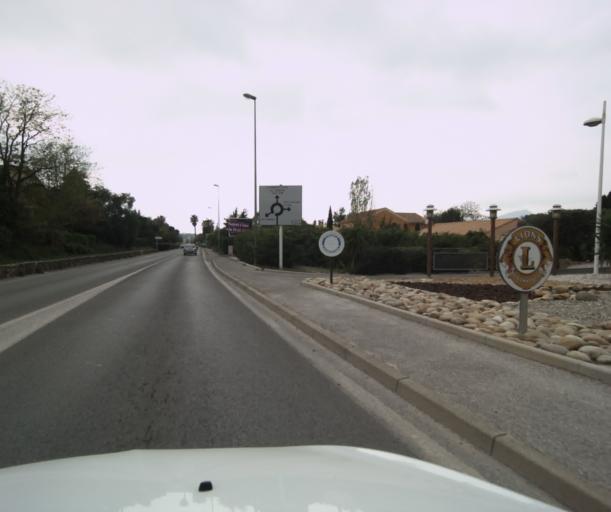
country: FR
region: Provence-Alpes-Cote d'Azur
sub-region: Departement du Var
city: Le Pradet
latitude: 43.1082
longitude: 6.0331
